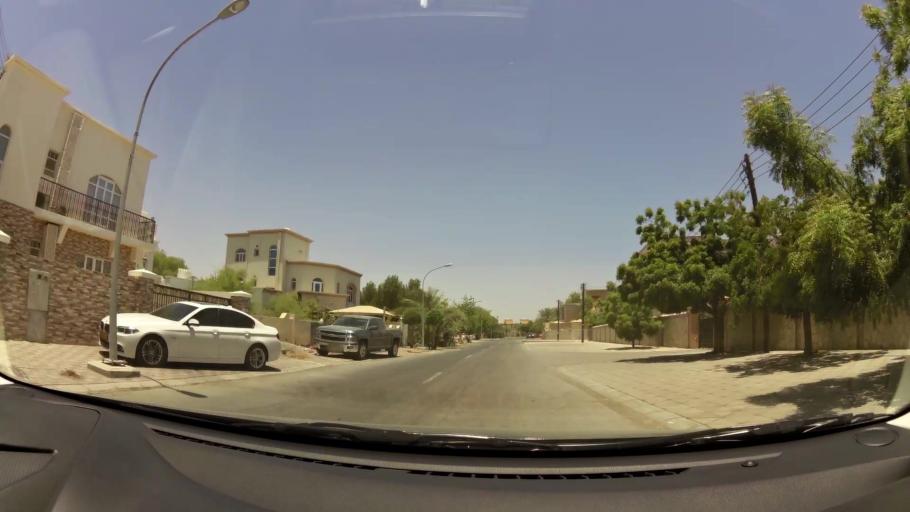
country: OM
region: Muhafazat Masqat
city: As Sib al Jadidah
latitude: 23.6359
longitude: 58.2364
